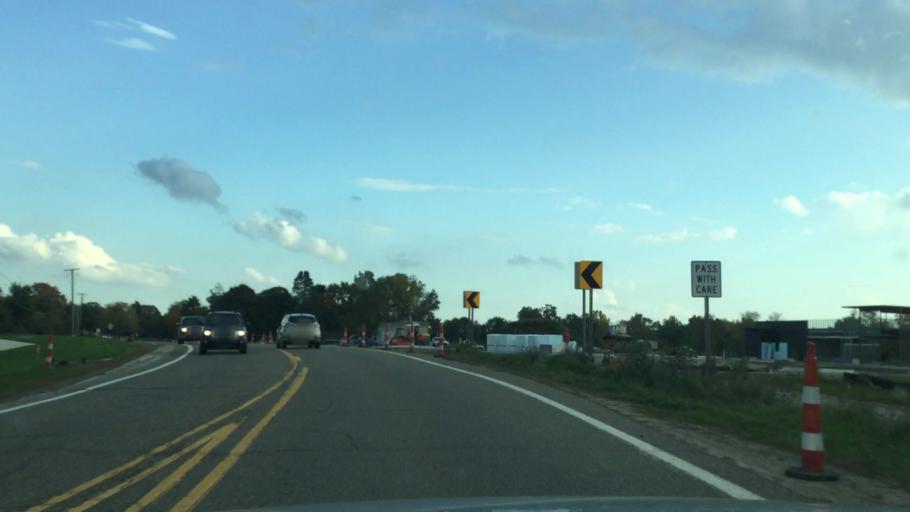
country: US
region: Michigan
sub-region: Oakland County
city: Wolverine Lake
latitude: 42.6469
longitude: -83.5036
